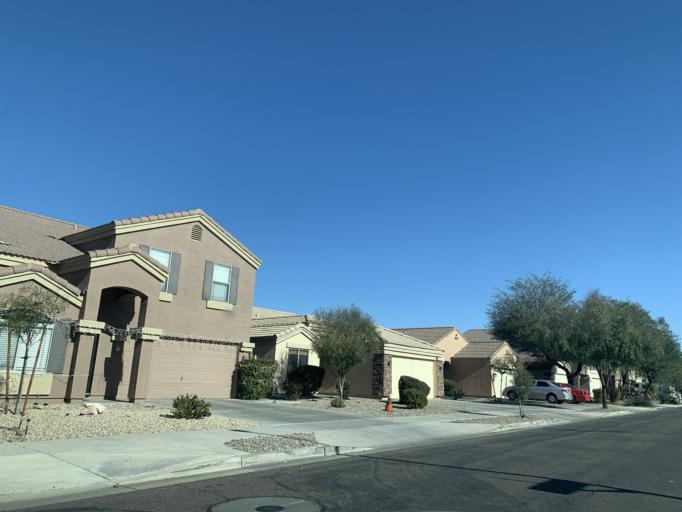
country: US
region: Arizona
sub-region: Maricopa County
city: Laveen
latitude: 33.3946
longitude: -112.1306
